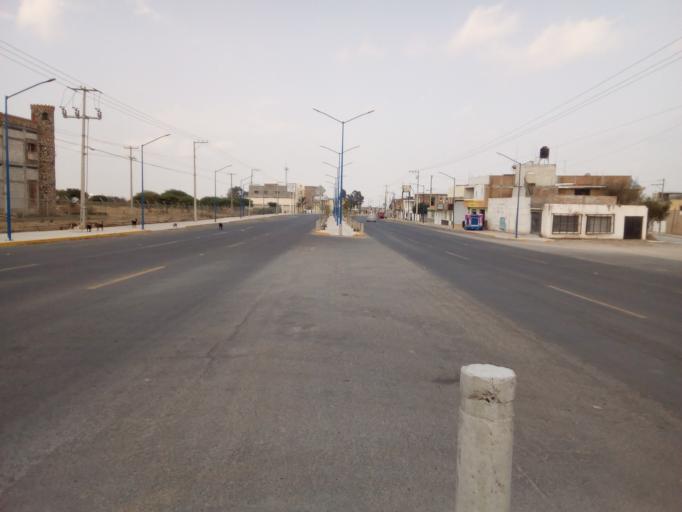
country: MX
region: Guerrero
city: San Luis de la Paz
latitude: 21.2882
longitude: -100.5176
